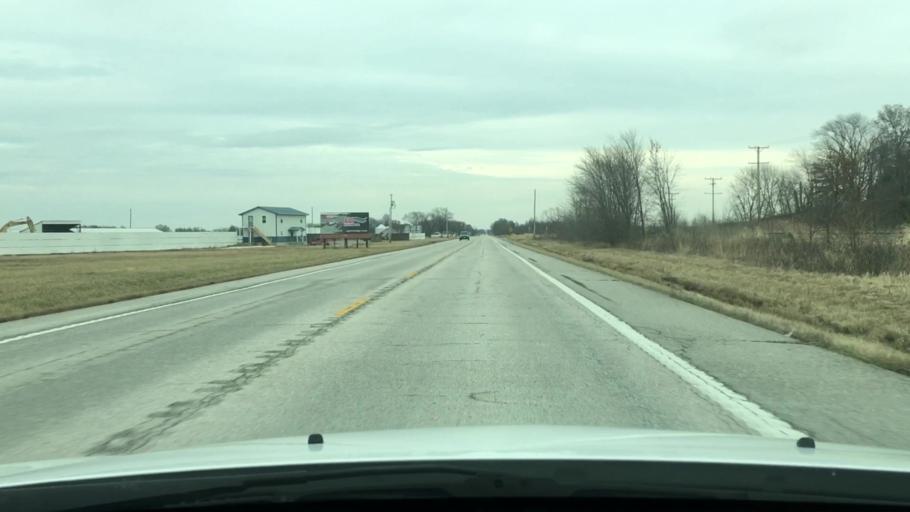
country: US
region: Missouri
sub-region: Audrain County
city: Vandalia
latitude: 39.2911
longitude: -91.5314
